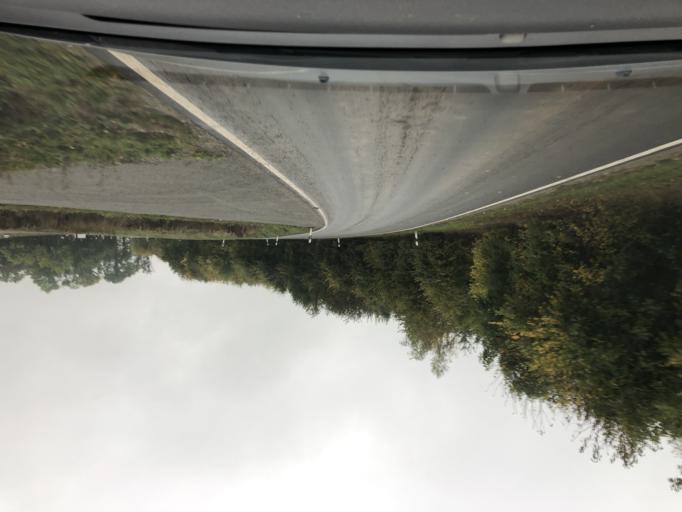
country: DE
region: Thuringia
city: Kreuzebra
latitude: 51.3613
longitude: 10.2640
